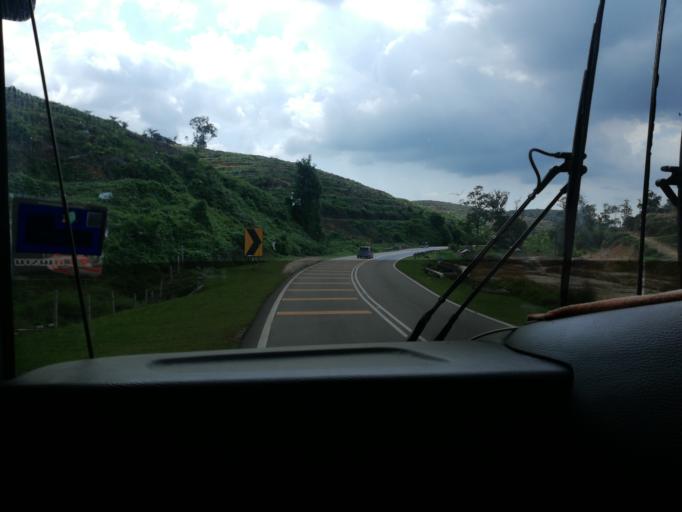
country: MY
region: Kedah
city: Kulim
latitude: 5.3087
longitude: 100.6105
